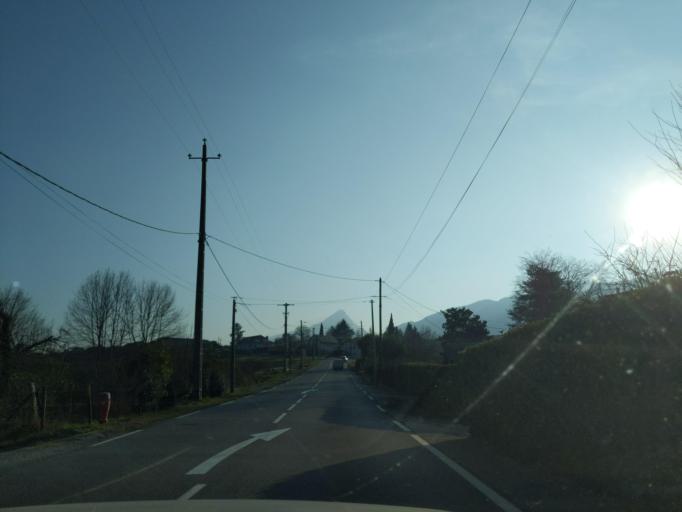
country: FR
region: Rhone-Alpes
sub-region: Departement de la Savoie
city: Brison-Saint-Innocent
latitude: 45.7343
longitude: 5.8909
